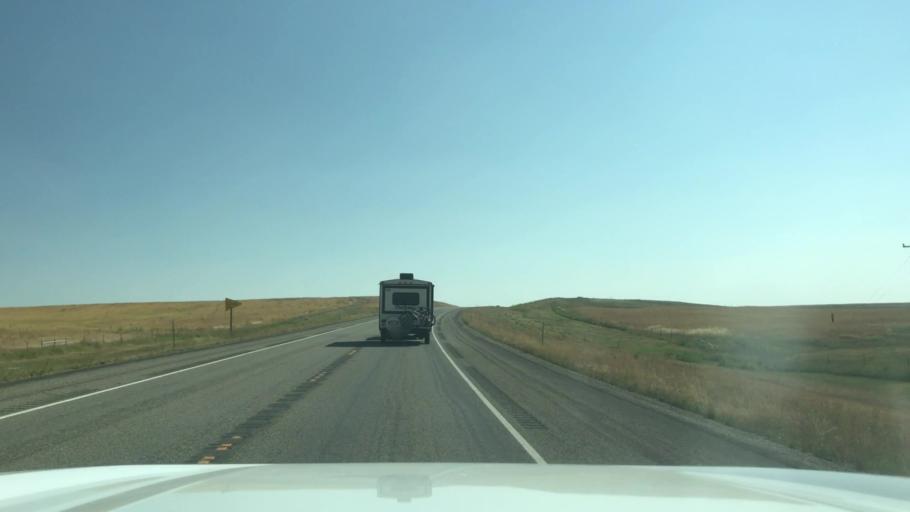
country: US
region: Montana
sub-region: Wheatland County
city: Harlowton
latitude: 46.4722
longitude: -109.7665
